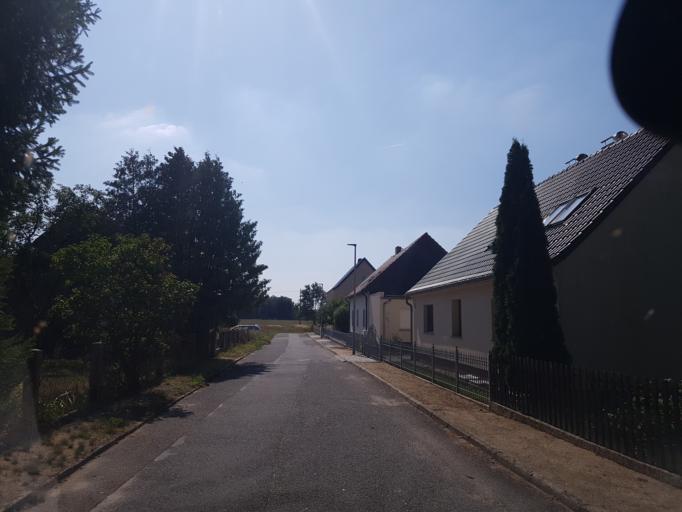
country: DE
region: Brandenburg
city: Hohenleipisch
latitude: 51.4844
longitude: 13.5402
